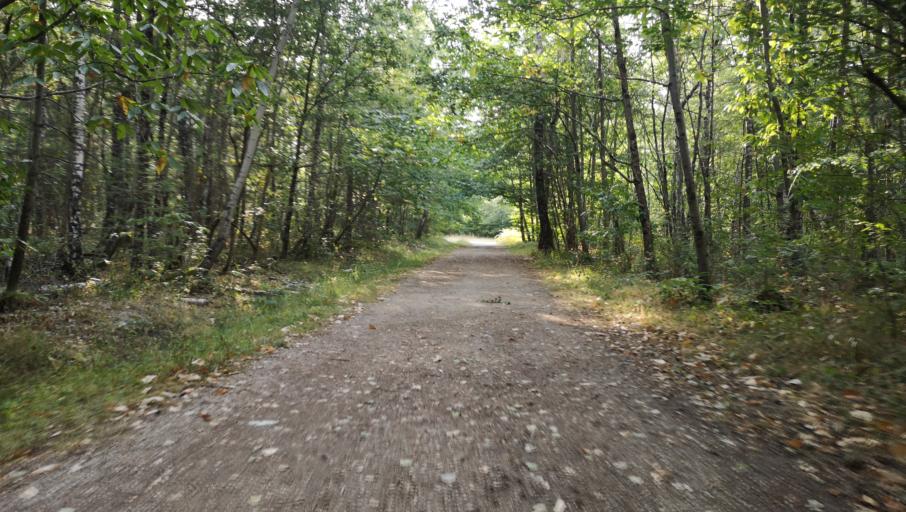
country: FR
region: Centre
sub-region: Departement du Loiret
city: Boigny-sur-Bionne
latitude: 47.9333
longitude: 1.9972
